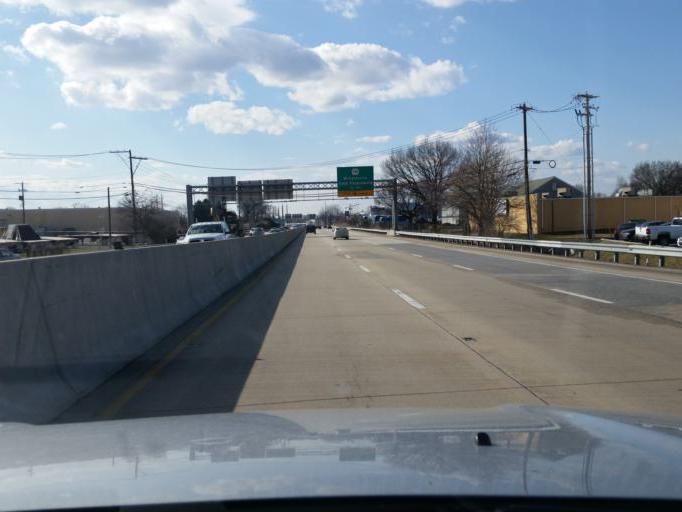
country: US
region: Pennsylvania
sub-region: Lancaster County
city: East Petersburg
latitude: 40.0771
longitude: -76.3392
